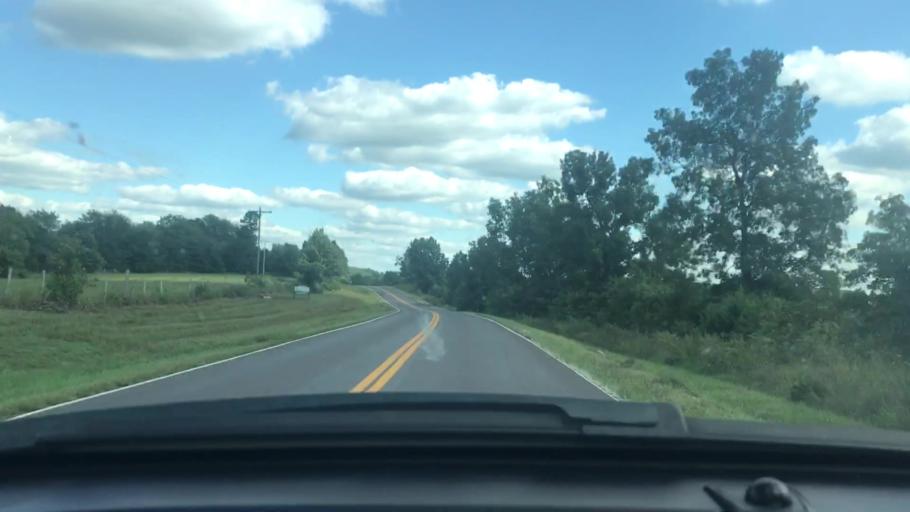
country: US
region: Missouri
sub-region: Wright County
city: Hartville
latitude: 37.3516
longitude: -92.3372
